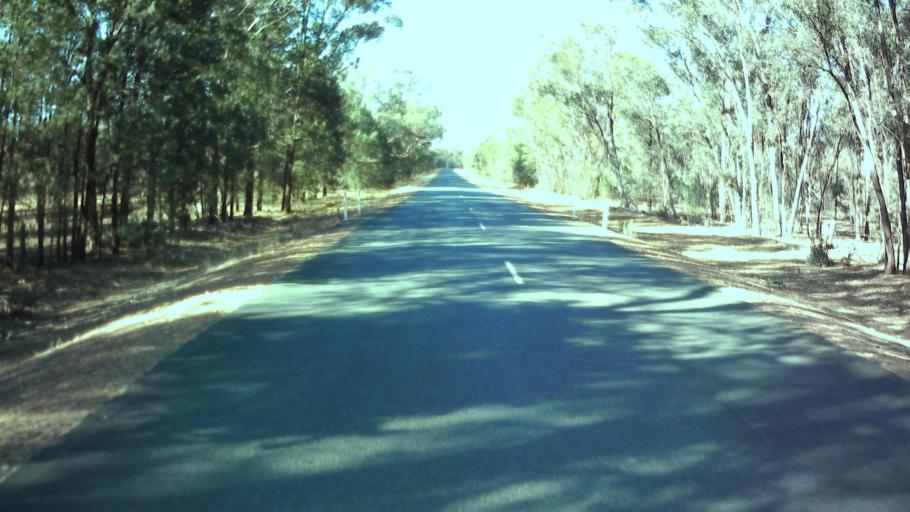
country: AU
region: New South Wales
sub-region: Weddin
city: Grenfell
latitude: -34.0255
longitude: 148.0974
